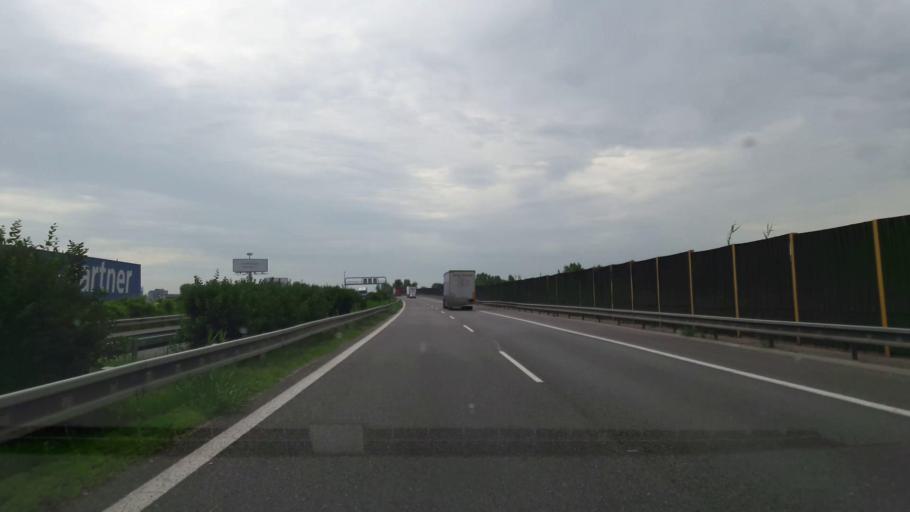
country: AT
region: Burgenland
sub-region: Politischer Bezirk Neusiedl am See
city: Kittsee
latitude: 48.1112
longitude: 17.0842
